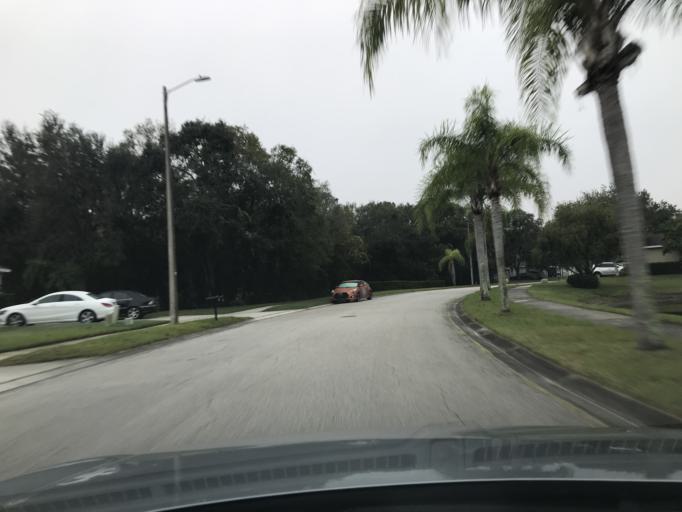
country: US
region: Florida
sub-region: Pinellas County
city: Oldsmar
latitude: 28.0485
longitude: -82.6649
